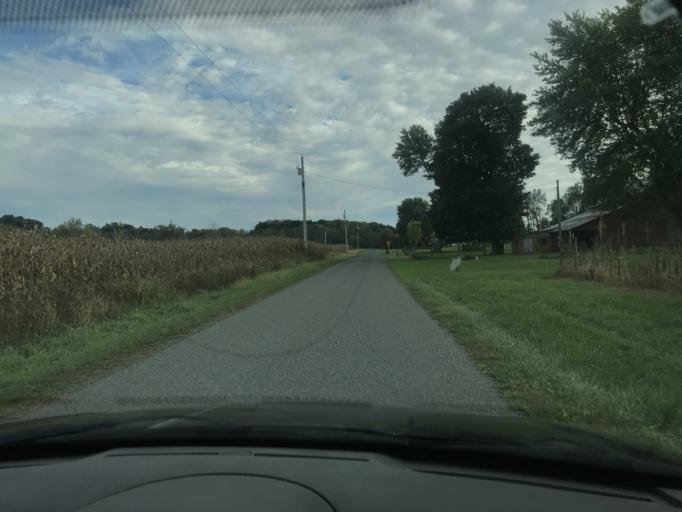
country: US
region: Ohio
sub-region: Logan County
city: West Liberty
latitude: 40.2498
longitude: -83.6951
